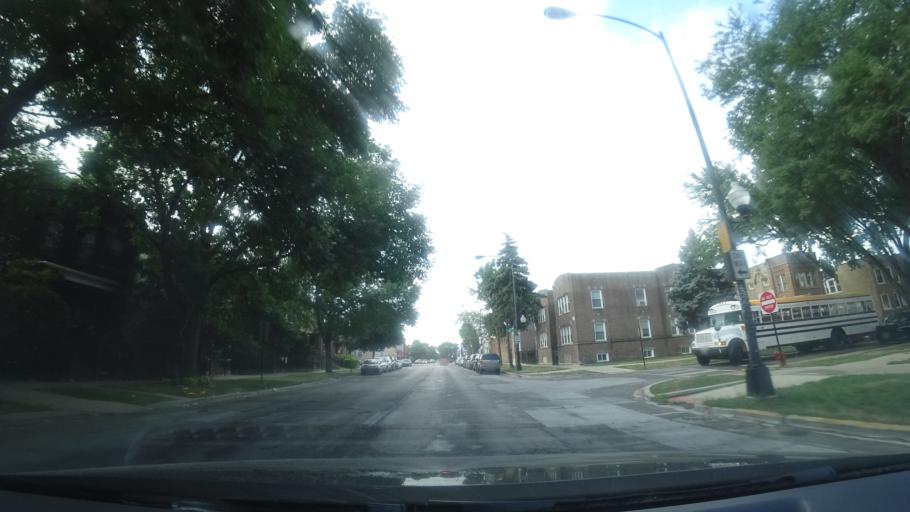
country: US
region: Illinois
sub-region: Cook County
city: Oak Park
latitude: 41.9256
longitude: -87.7366
